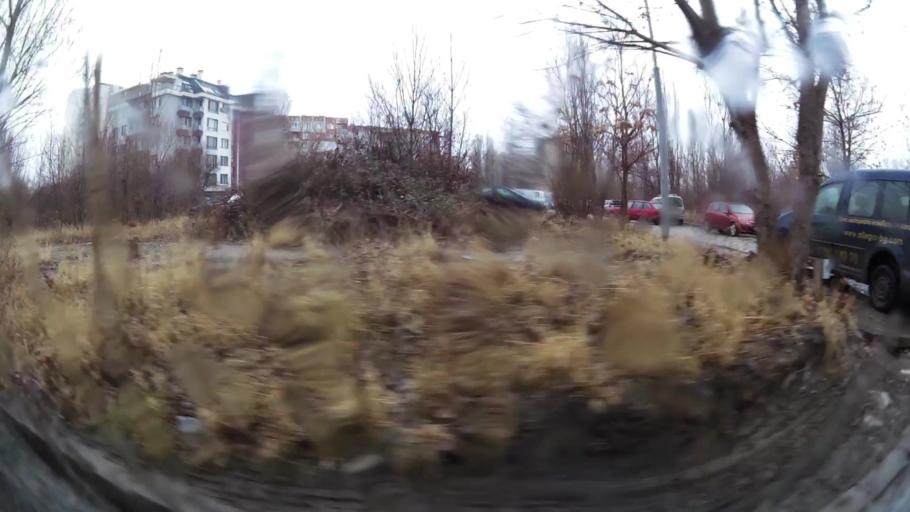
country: BG
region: Sofia-Capital
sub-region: Stolichna Obshtina
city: Sofia
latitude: 42.6641
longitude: 23.3835
